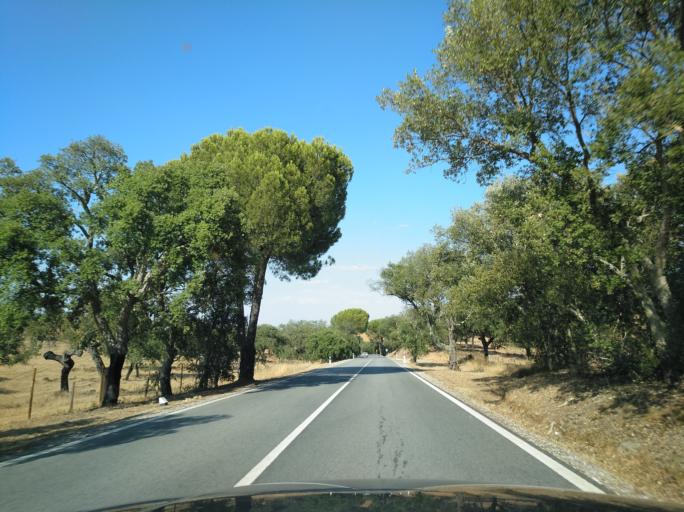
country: ES
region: Andalusia
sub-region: Provincia de Huelva
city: Rosal de la Frontera
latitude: 38.0116
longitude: -7.2722
